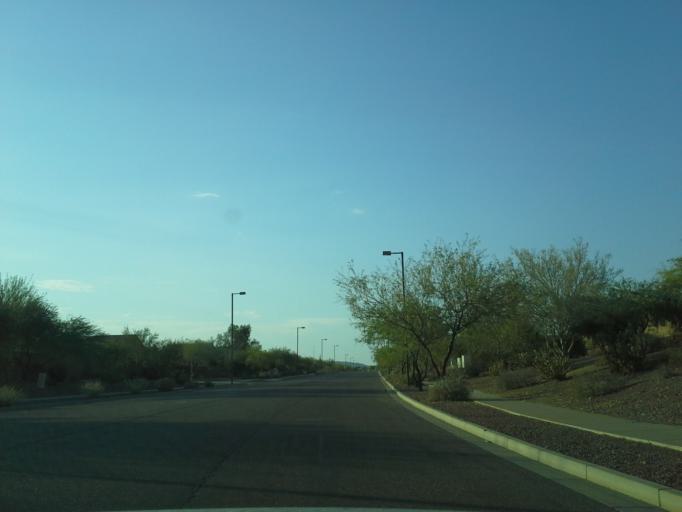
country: US
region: Arizona
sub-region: Maricopa County
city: Anthem
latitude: 33.8683
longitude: -112.1561
